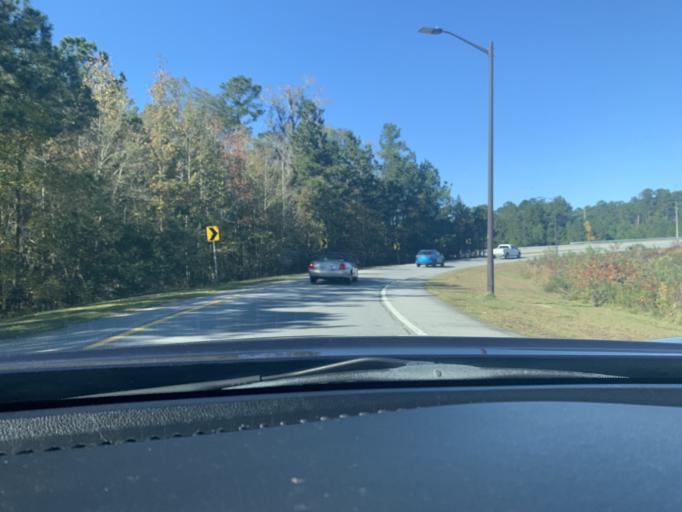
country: US
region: Georgia
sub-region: Chatham County
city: Pooler
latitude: 32.1187
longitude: -81.2678
